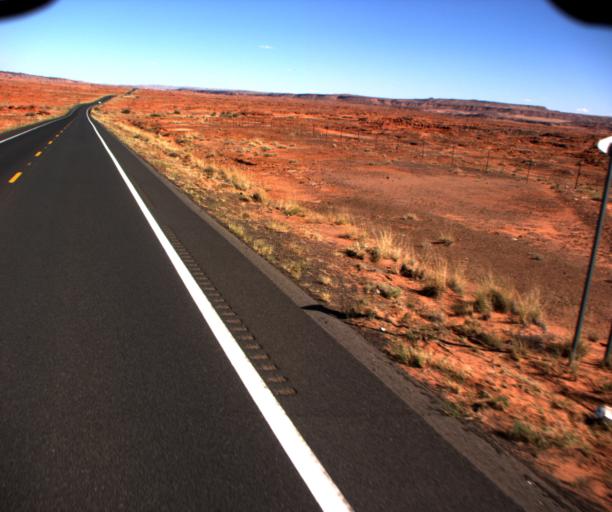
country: US
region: Arizona
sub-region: Coconino County
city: Tuba City
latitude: 36.0982
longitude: -111.3443
